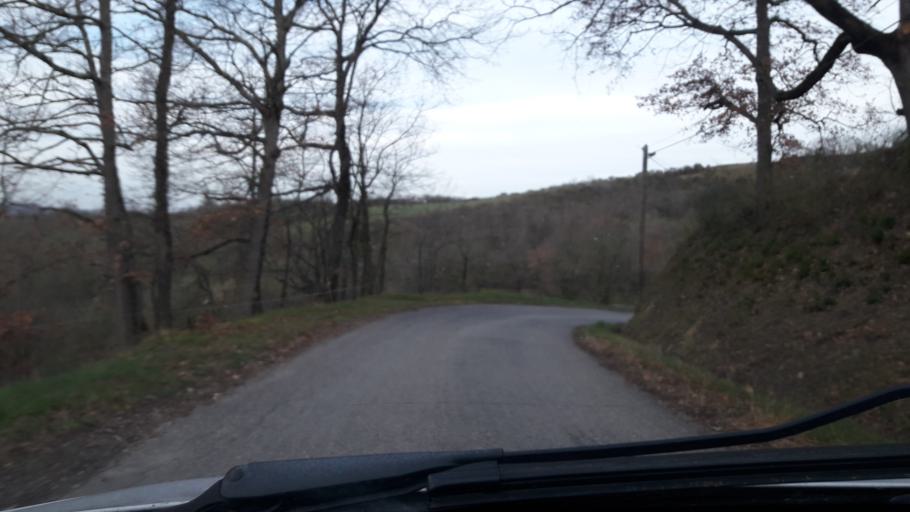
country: FR
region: Midi-Pyrenees
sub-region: Departement de la Haute-Garonne
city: Montesquieu-Volvestre
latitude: 43.1765
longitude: 1.2898
